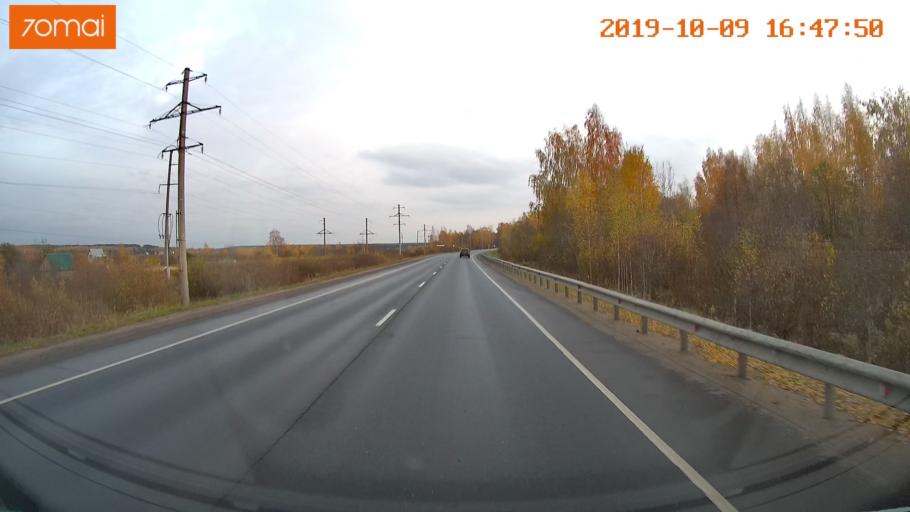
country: RU
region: Kostroma
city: Volgorechensk
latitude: 57.4345
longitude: 41.1829
